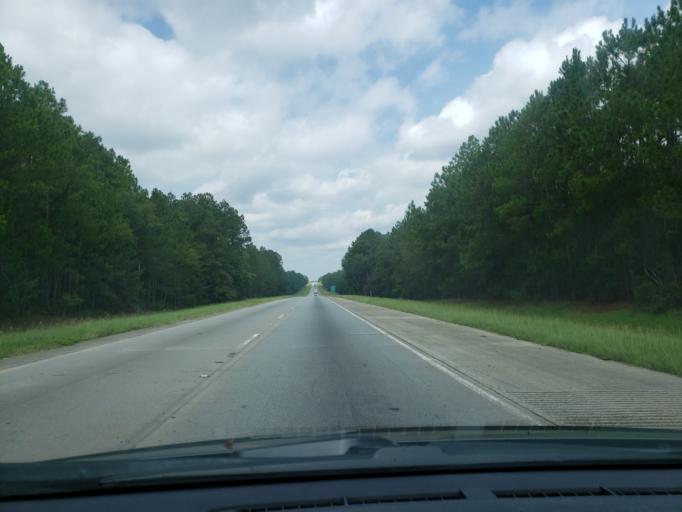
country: US
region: Georgia
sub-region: Emanuel County
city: Swainsboro
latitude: 32.4124
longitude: -82.3663
